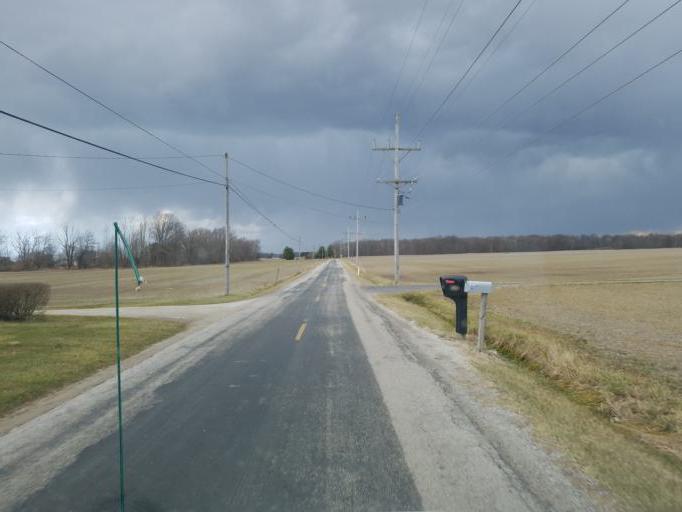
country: US
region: Ohio
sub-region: Marion County
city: Prospect
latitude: 40.4654
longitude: -83.1114
